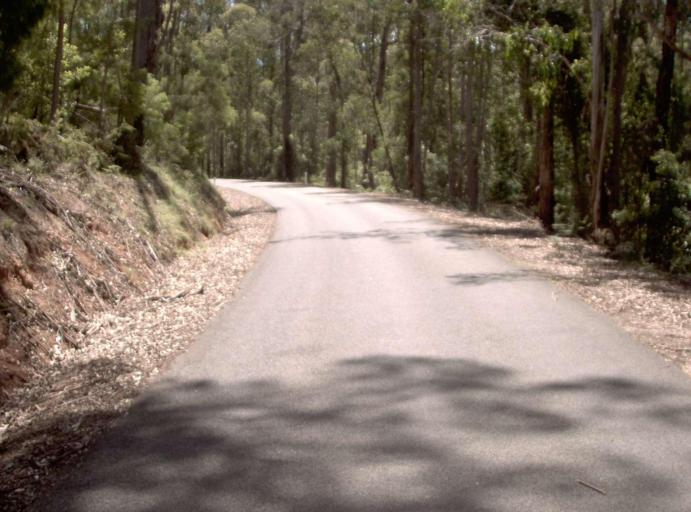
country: AU
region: New South Wales
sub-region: Bombala
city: Bombala
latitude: -37.5070
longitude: 148.9279
